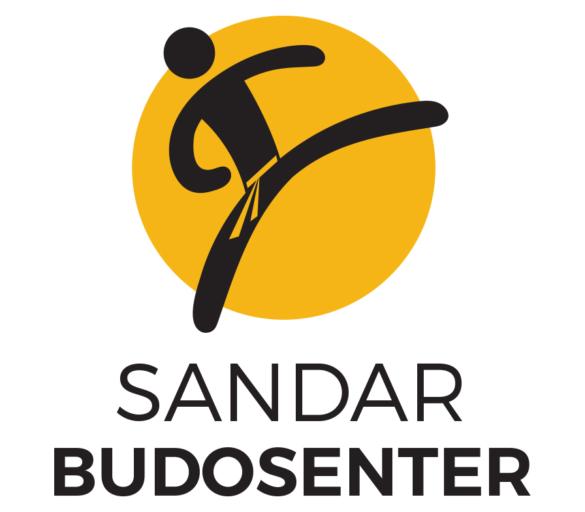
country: NO
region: Vestfold
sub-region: Sandefjord
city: Sandefjord
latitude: 59.1108
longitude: 10.2532
